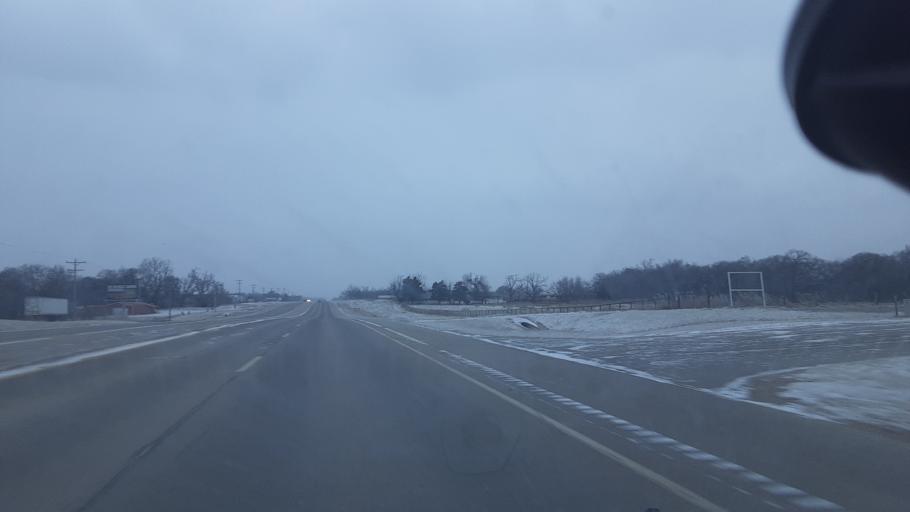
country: US
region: Oklahoma
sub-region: Payne County
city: Perkins
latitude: 35.9855
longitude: -97.0610
